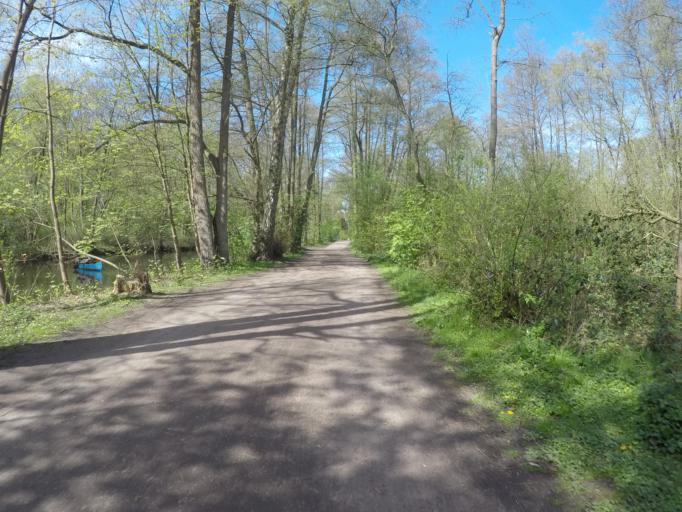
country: DE
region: Hamburg
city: Ohlsdorf
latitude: 53.6308
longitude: 10.0344
